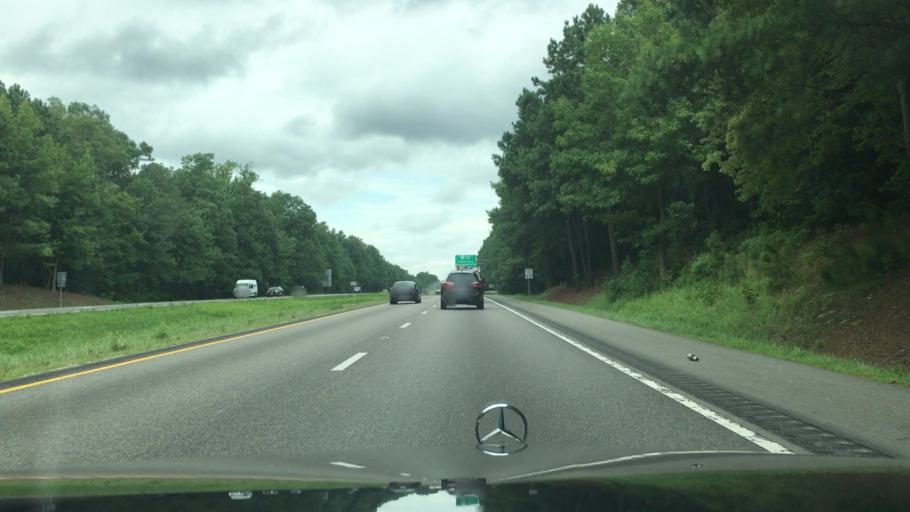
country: US
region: Virginia
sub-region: Chesterfield County
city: Brandermill
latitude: 37.4338
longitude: -77.6338
